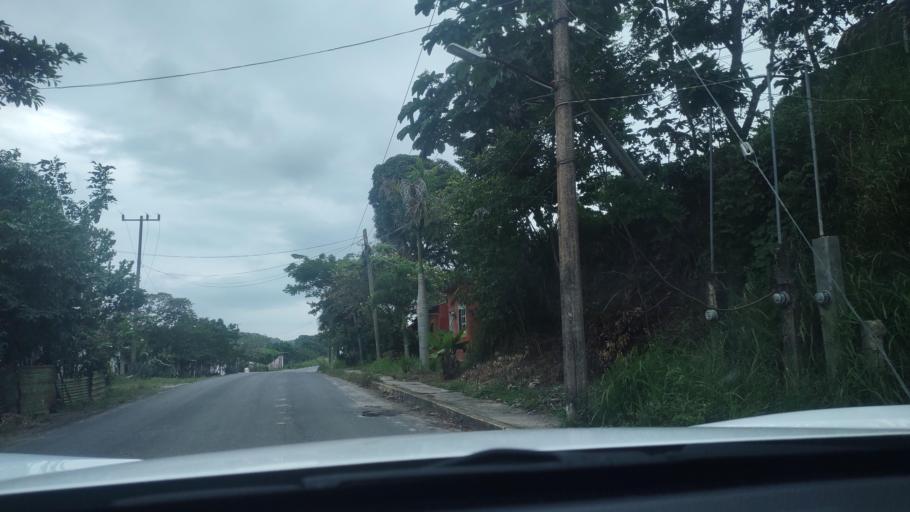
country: MX
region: Veracruz
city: Villa Nanchital
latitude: 18.0460
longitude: -94.3556
